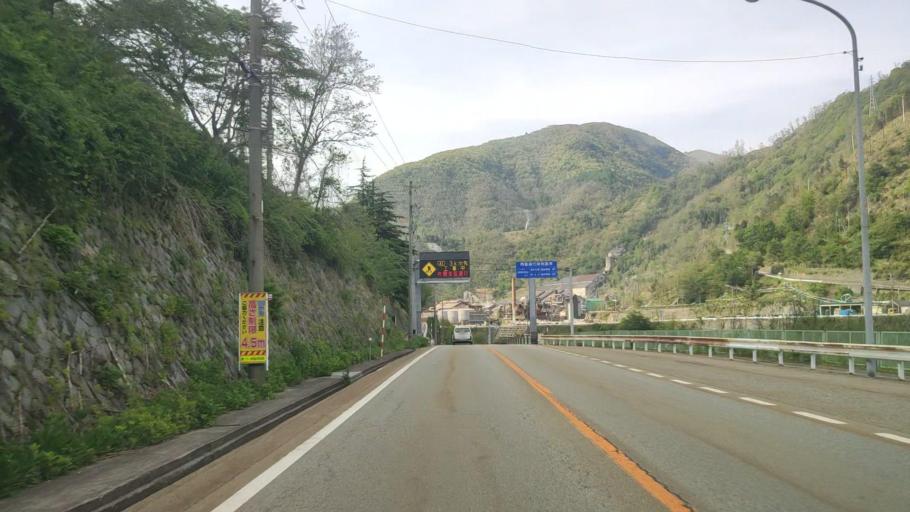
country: JP
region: Gifu
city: Takayama
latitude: 36.3421
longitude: 137.2949
